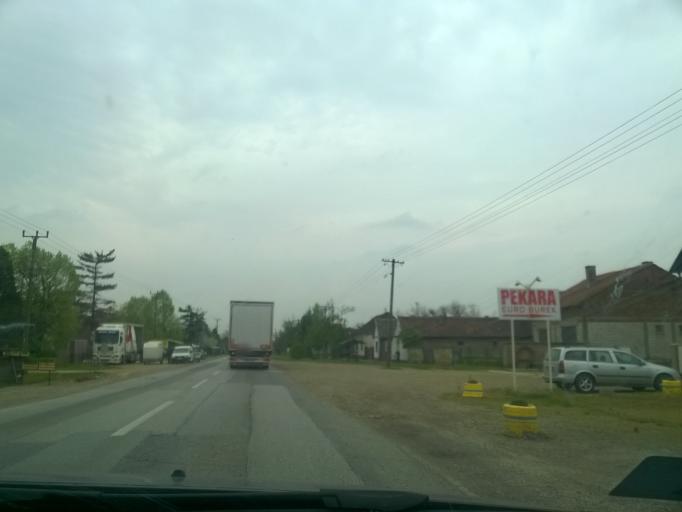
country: RS
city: Hrtkovci
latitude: 44.8881
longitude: 19.7637
